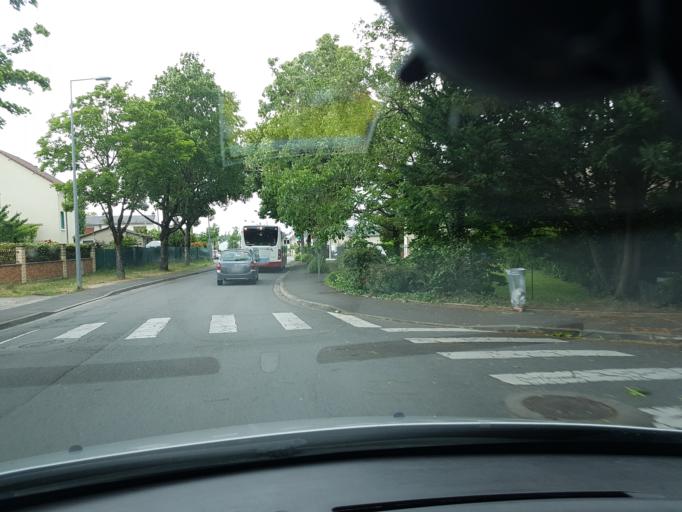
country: FR
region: Centre
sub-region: Departement du Cher
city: Bourges
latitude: 47.1104
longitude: 2.4154
